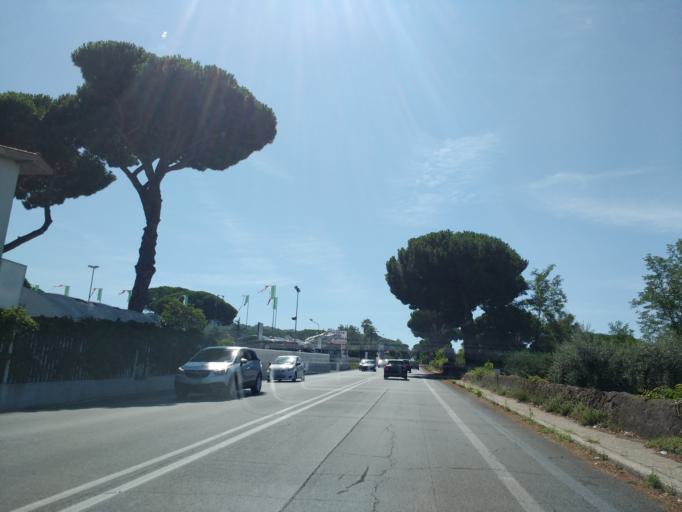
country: IT
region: Latium
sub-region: Citta metropolitana di Roma Capitale
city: Marino
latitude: 41.7551
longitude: 12.6293
